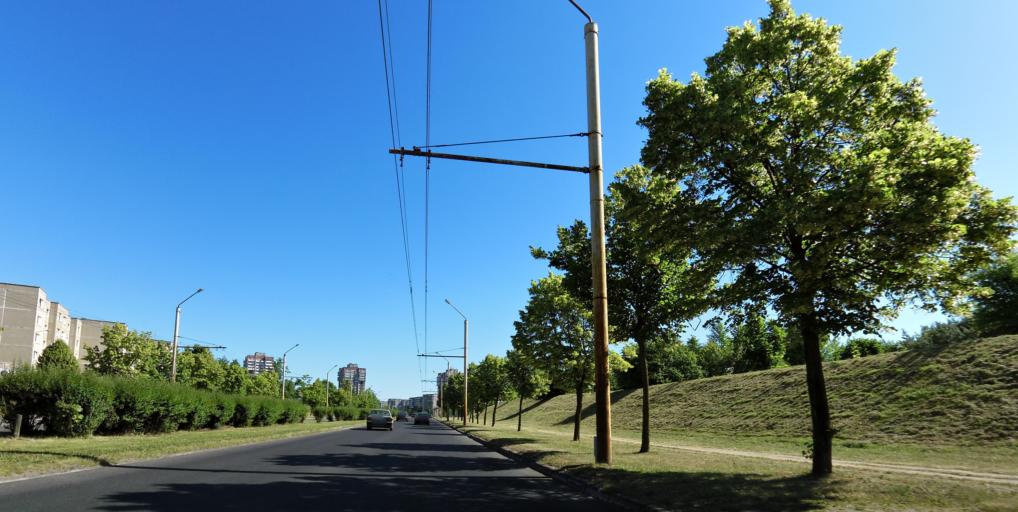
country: LT
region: Vilnius County
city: Justiniskes
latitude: 54.7141
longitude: 25.2194
